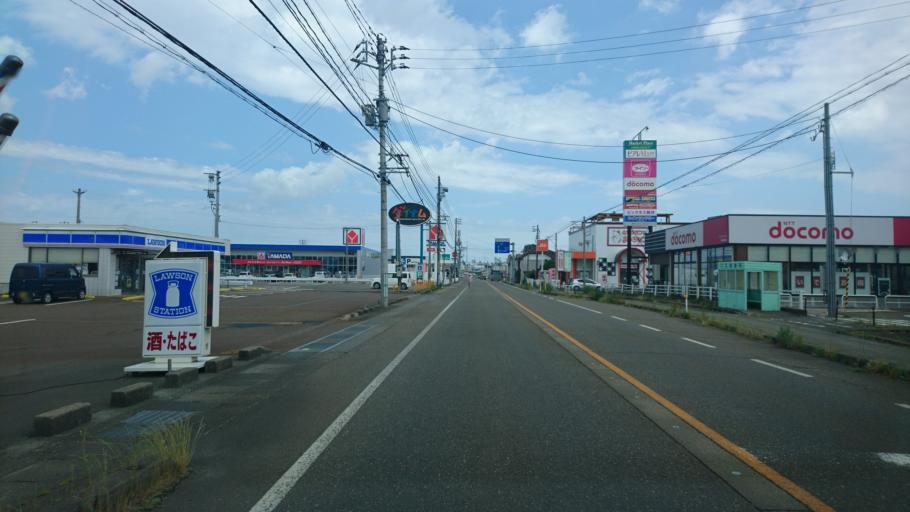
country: JP
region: Niigata
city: Arai
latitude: 37.0539
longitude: 138.2605
